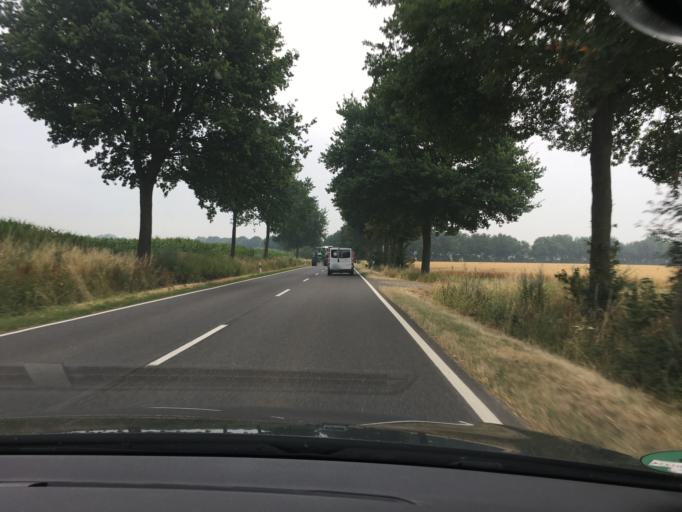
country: DE
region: North Rhine-Westphalia
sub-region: Regierungsbezirk Koln
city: Titz
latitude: 51.0351
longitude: 6.3938
